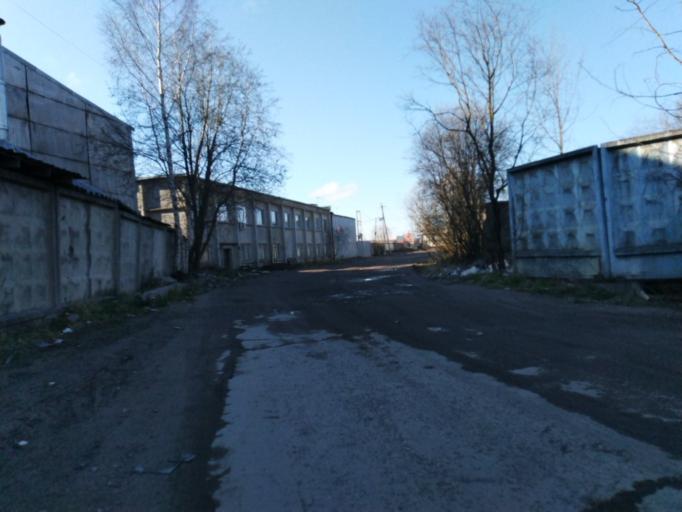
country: RU
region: Leningrad
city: Novoye Devyatkino
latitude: 60.0695
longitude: 30.4930
